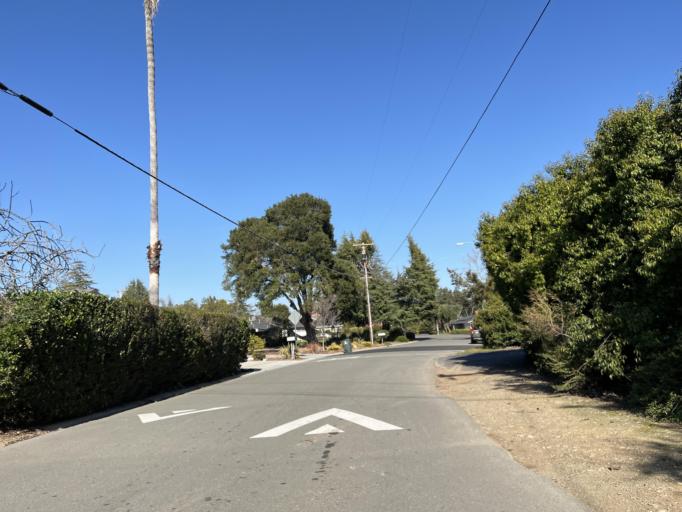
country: US
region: California
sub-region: Santa Clara County
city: Cupertino
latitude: 37.3187
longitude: -122.0641
